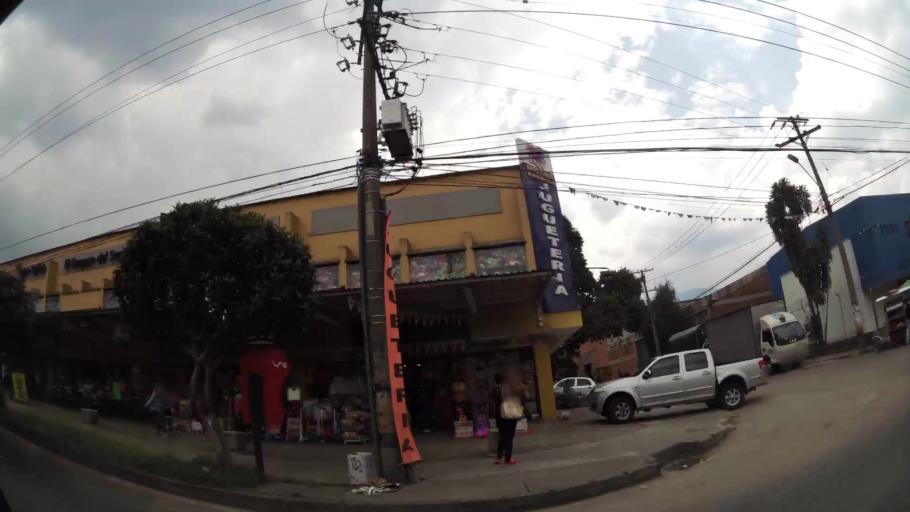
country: CO
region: Antioquia
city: Sabaneta
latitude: 6.1662
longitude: -75.6069
